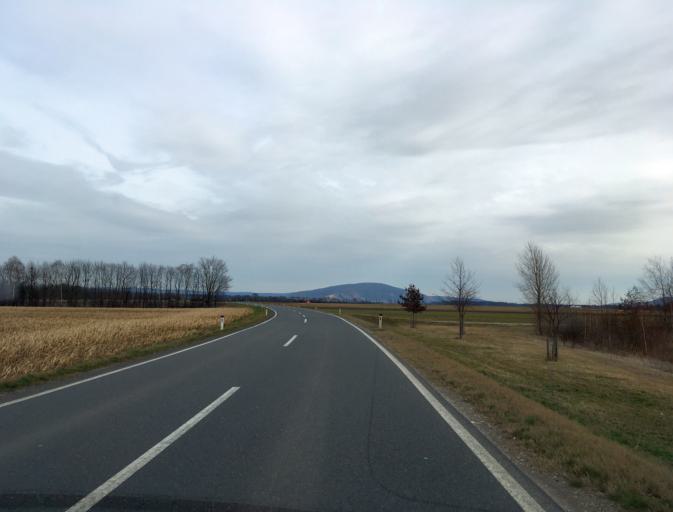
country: AT
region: Lower Austria
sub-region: Politischer Bezirk Ganserndorf
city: Lassee
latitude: 48.2228
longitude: 16.8614
